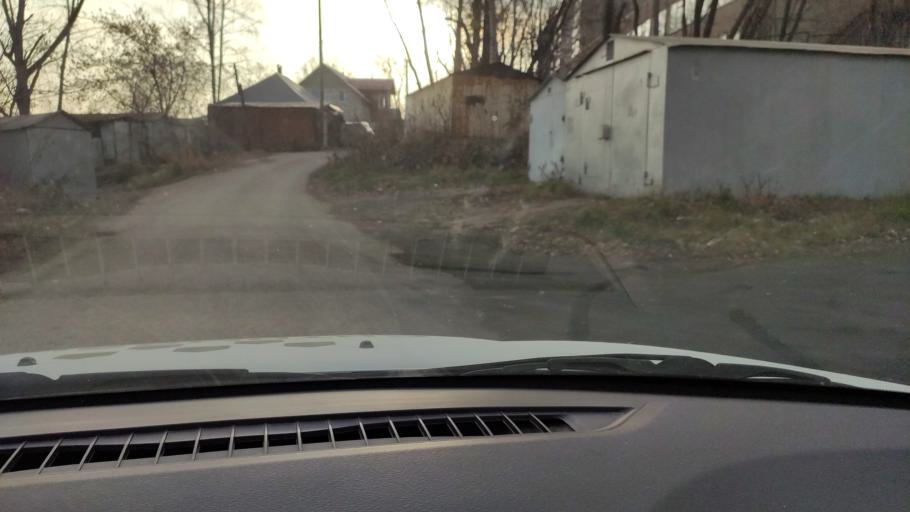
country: RU
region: Perm
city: Perm
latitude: 58.0233
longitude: 56.3052
